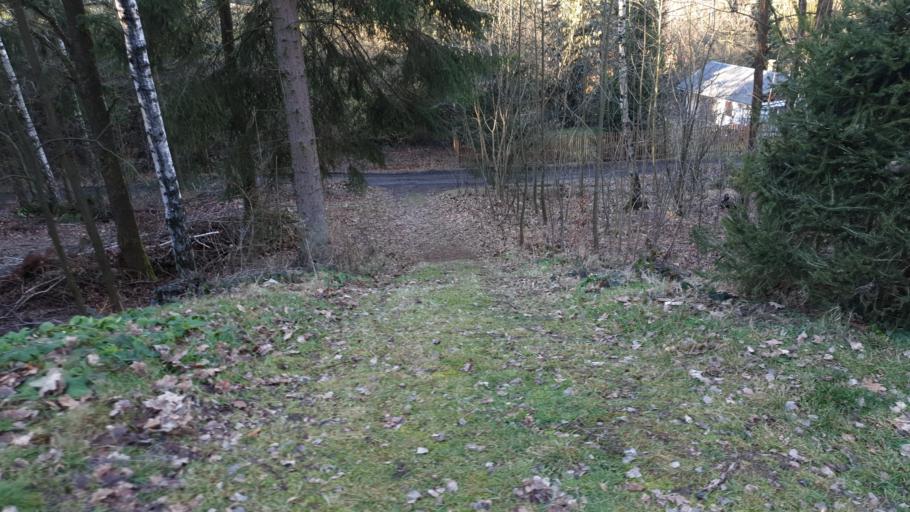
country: DE
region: Saxony
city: Gelenau
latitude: 50.7625
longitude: 12.9822
